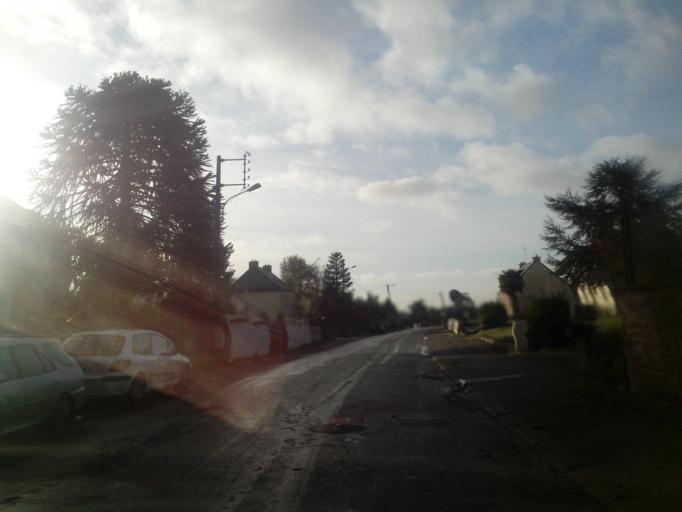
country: FR
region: Brittany
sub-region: Departement du Morbihan
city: Meneac
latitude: 48.1373
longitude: -2.4611
